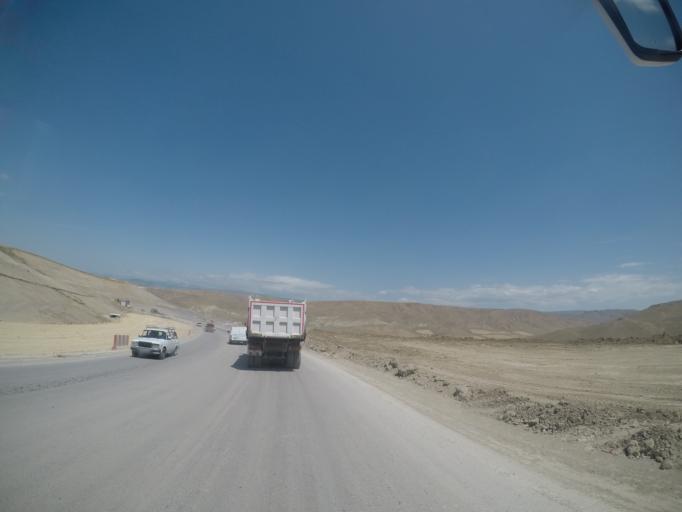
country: AZ
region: Samaxi
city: Shamakhi
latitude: 40.5484
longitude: 48.7719
